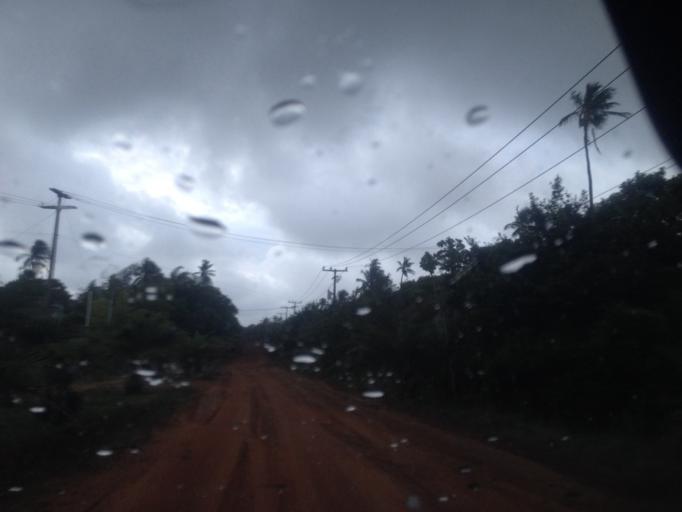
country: BR
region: Bahia
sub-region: Mata De Sao Joao
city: Mata de Sao Joao
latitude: -12.5739
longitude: -38.0257
